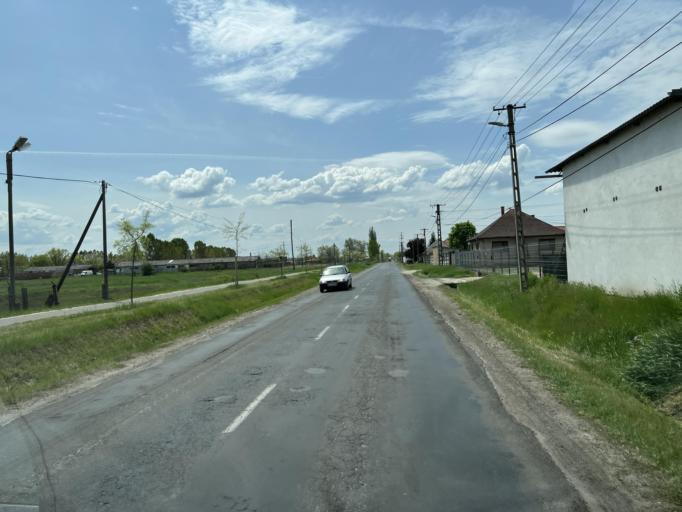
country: HU
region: Pest
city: Cegled
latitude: 47.1603
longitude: 19.7746
